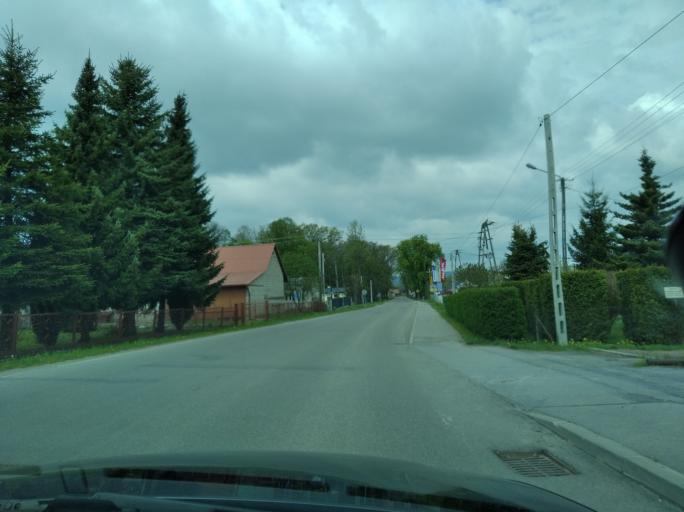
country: PL
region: Subcarpathian Voivodeship
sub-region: Powiat brzozowski
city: Haczow
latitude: 49.6685
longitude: 21.8966
